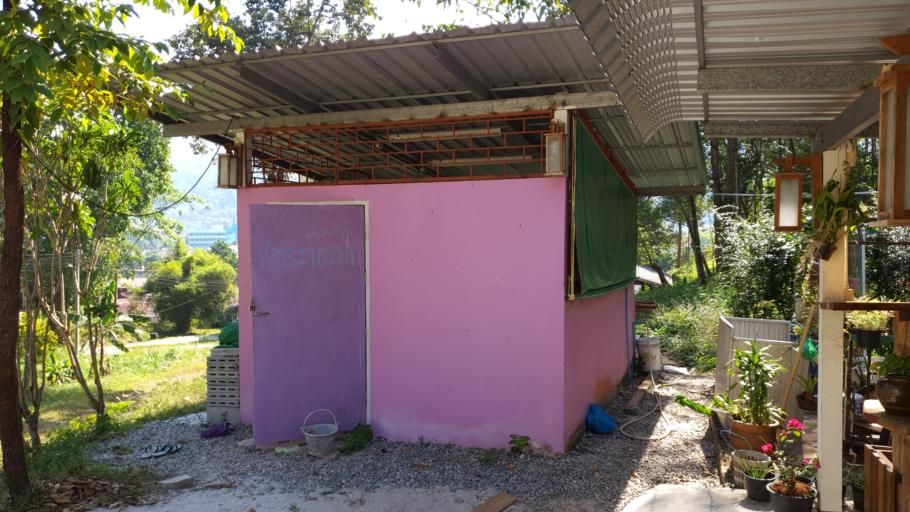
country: TH
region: Ranong
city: Ranong
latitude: 9.9646
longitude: 98.6379
